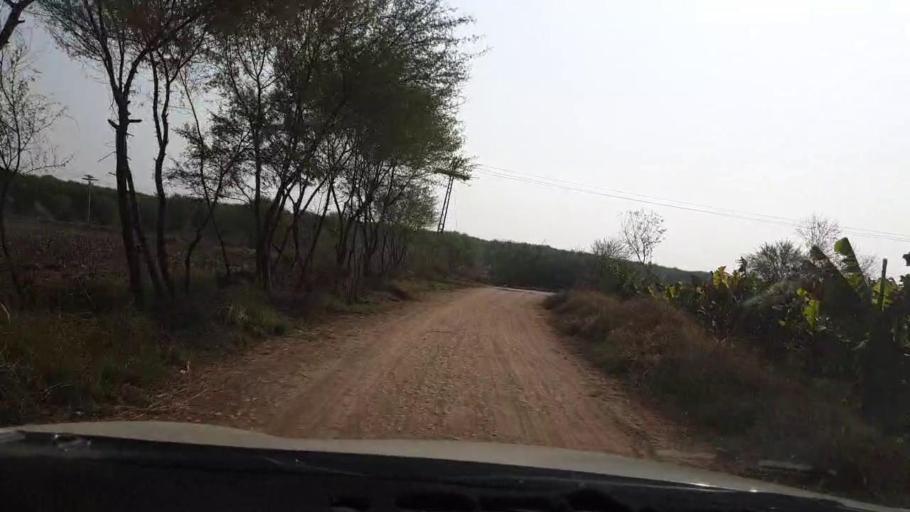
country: PK
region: Sindh
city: Matiari
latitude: 25.6232
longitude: 68.4980
